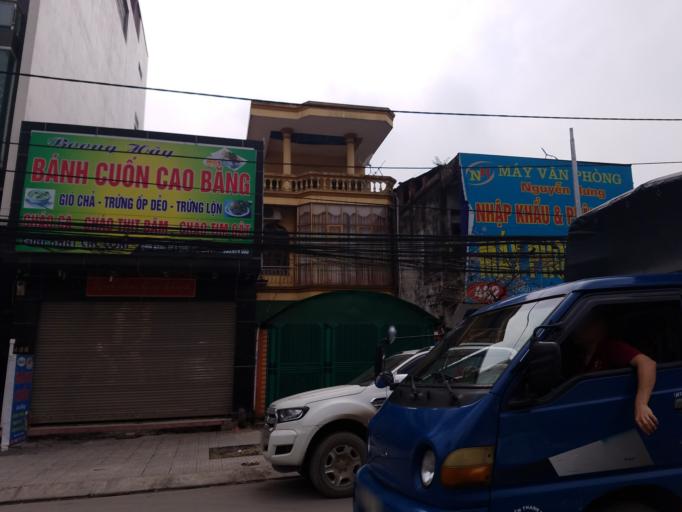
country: VN
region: Thai Nguyen
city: Thanh Pho Thai Nguyen
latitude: 21.5852
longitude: 105.8328
